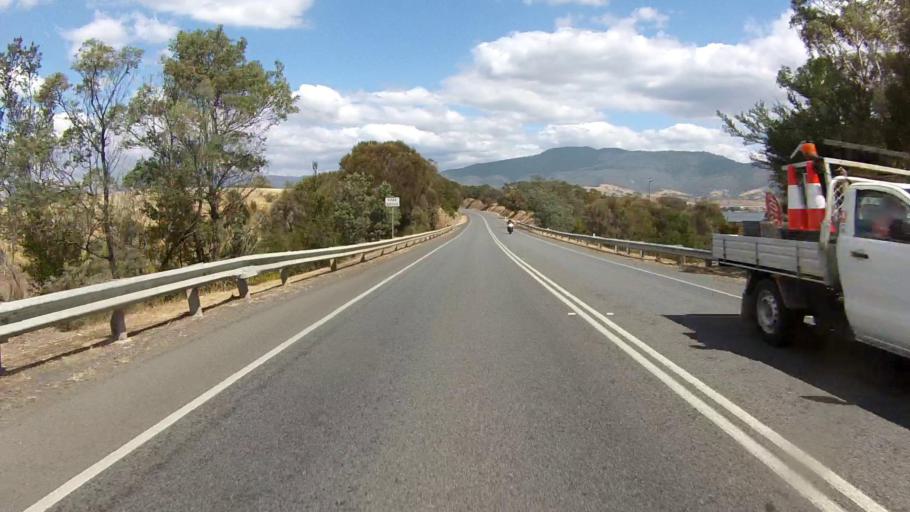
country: AU
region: Tasmania
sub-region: Brighton
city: Old Beach
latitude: -42.7544
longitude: 147.2709
